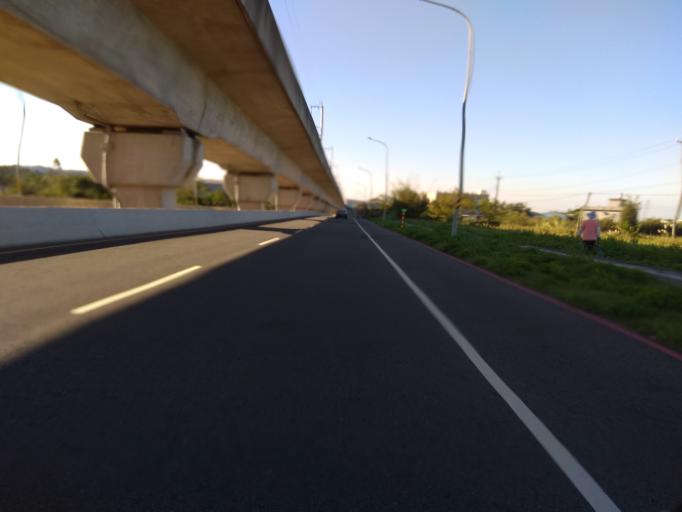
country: TW
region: Taiwan
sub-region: Hsinchu
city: Zhubei
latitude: 24.9005
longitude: 121.0816
